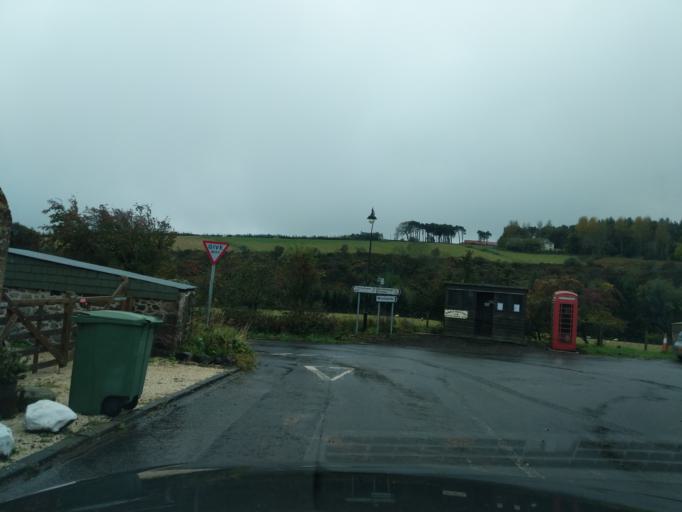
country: GB
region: Scotland
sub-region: East Lothian
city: Dunbar
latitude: 55.9275
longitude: -2.4135
